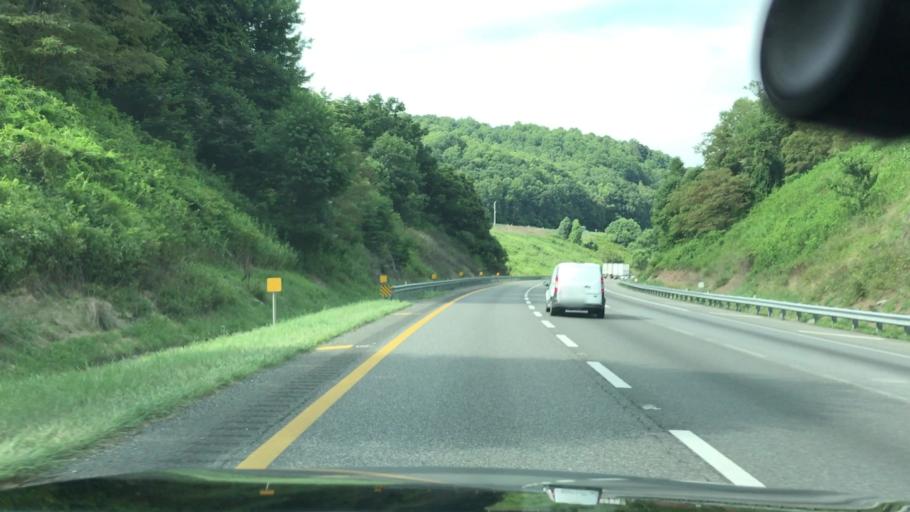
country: US
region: Virginia
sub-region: Carroll County
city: Cana
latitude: 36.6175
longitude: -80.7397
